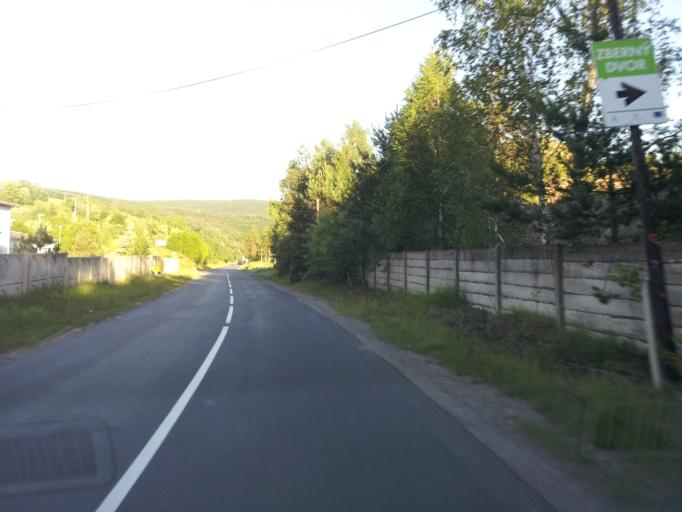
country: SK
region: Banskobystricky
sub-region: Okres Banska Bystrica
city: Banska Stiavnica
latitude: 48.4356
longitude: 18.9246
